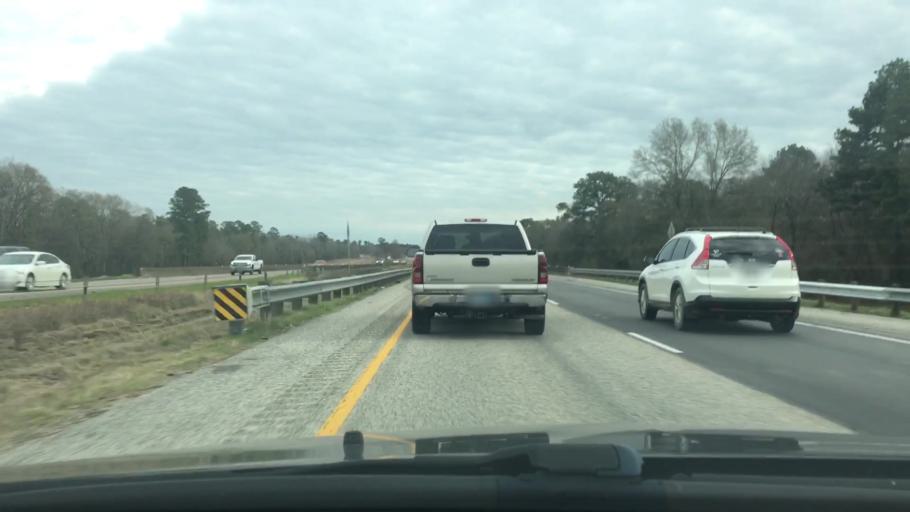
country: US
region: Texas
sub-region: Walker County
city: Huntsville
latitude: 30.7901
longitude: -95.6711
